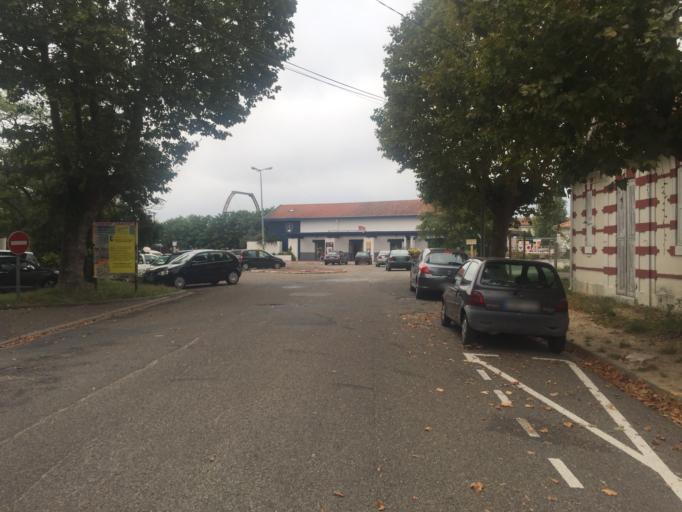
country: FR
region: Aquitaine
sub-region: Departement de la Gironde
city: La Teste-de-Buch
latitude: 44.6363
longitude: -1.1427
